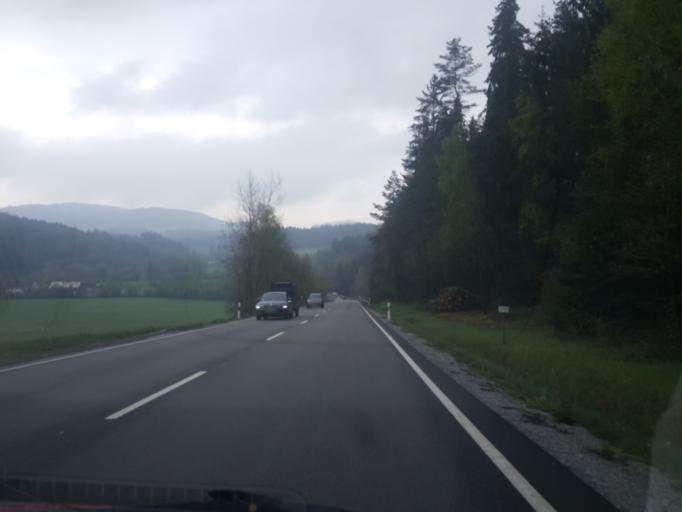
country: DE
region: Bavaria
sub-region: Lower Bavaria
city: Viechtach
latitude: 49.0593
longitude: 12.9086
